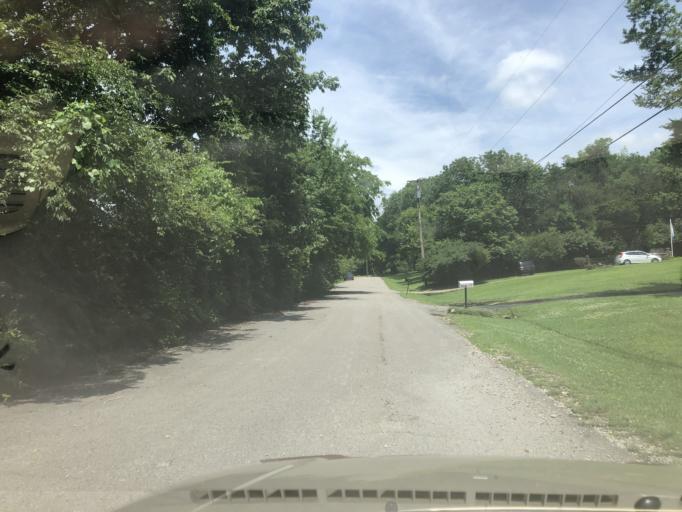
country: US
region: Tennessee
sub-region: Davidson County
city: Lakewood
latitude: 36.2440
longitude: -86.6820
